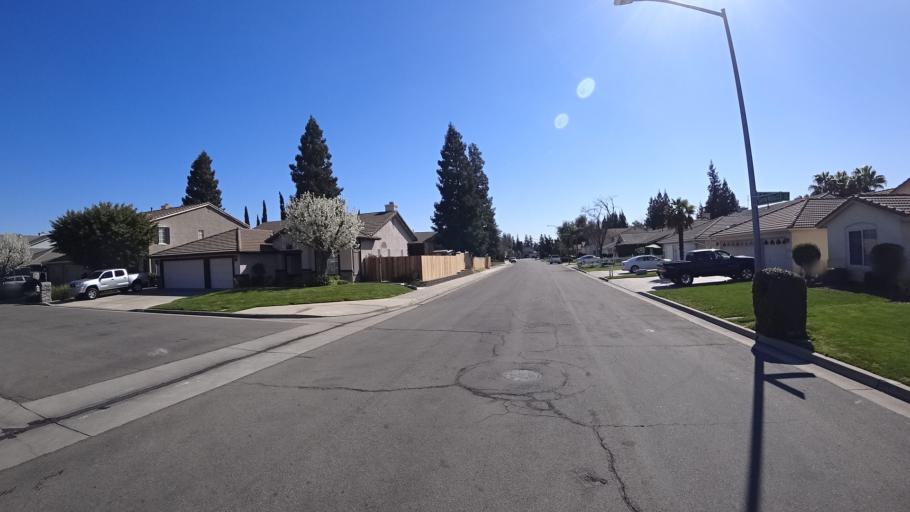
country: US
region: California
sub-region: Fresno County
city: Clovis
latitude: 36.8655
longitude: -119.7440
